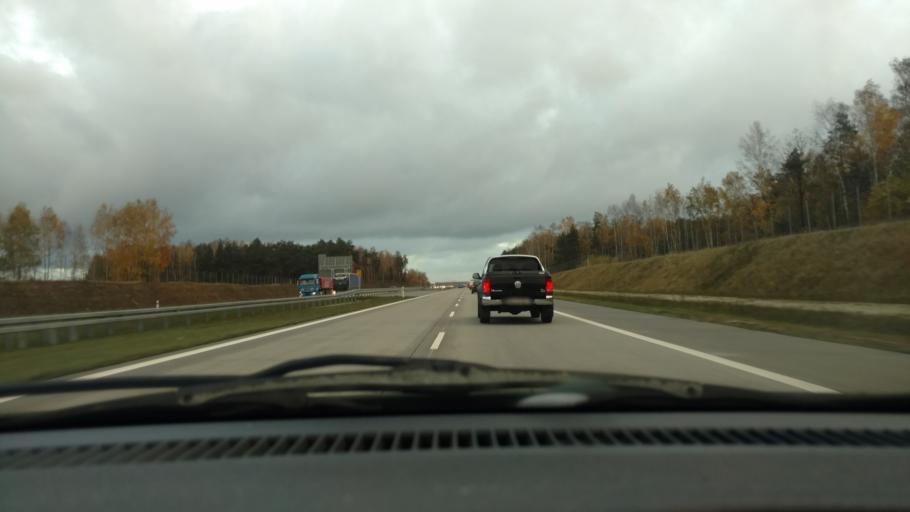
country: PL
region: Lodz Voivodeship
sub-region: Powiat lodzki wschodni
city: Brojce
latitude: 51.6617
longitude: 19.5830
